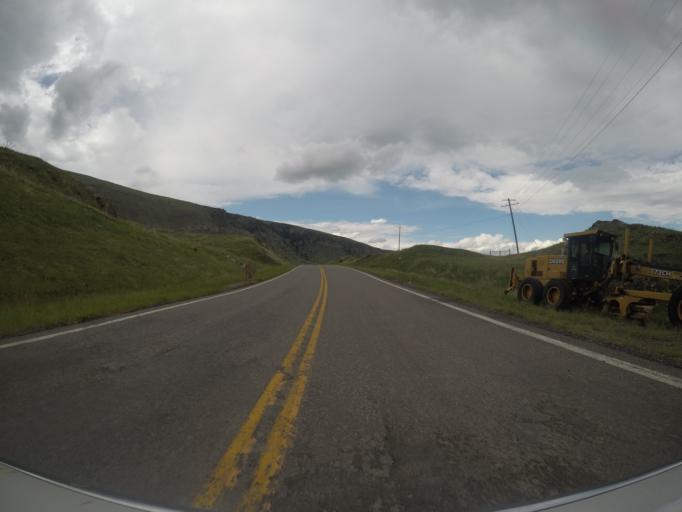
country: US
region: Montana
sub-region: Sweet Grass County
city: Big Timber
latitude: 45.5656
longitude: -110.2017
